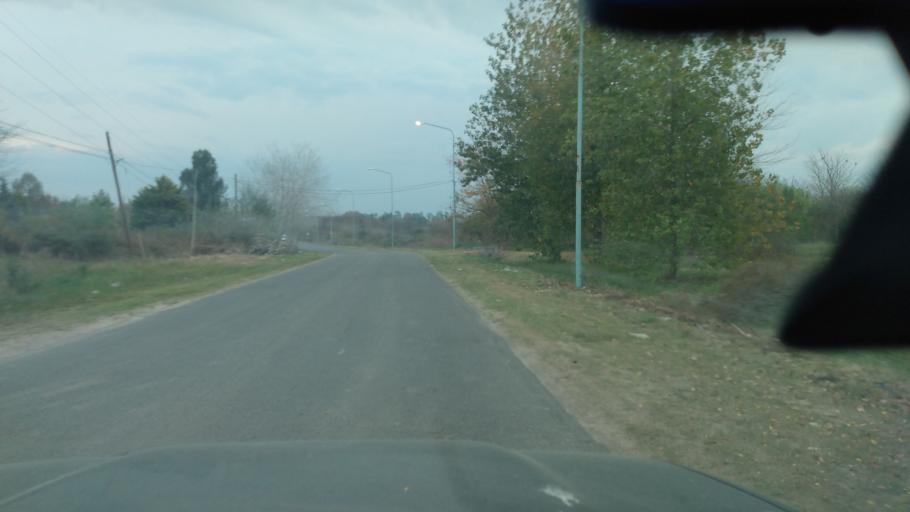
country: AR
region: Buenos Aires
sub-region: Partido de Lujan
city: Lujan
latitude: -34.5662
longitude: -59.1450
